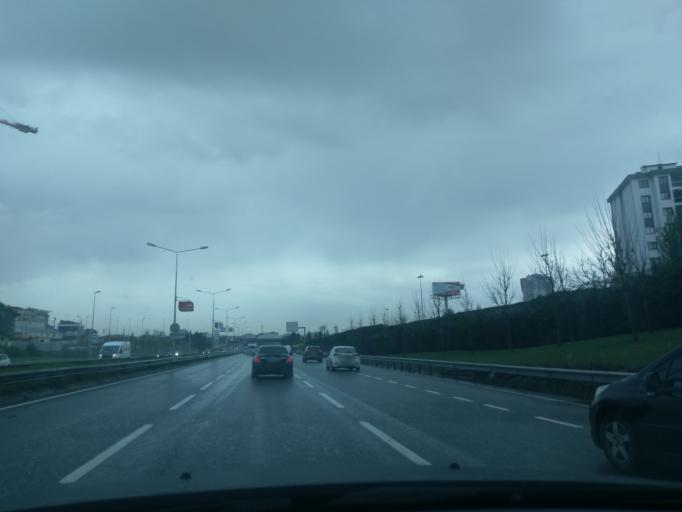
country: TR
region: Istanbul
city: Samandira
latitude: 41.0188
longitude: 29.1813
